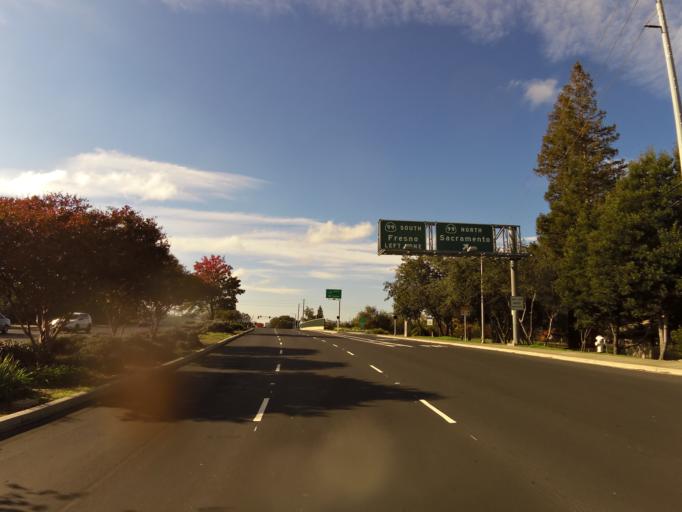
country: US
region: California
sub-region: Sacramento County
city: Elk Grove
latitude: 38.4093
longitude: -121.3871
